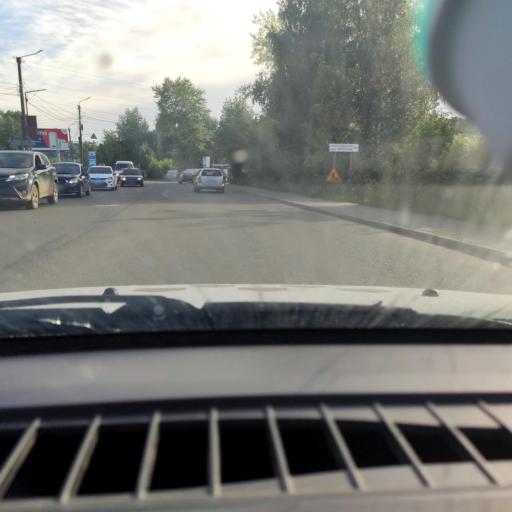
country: RU
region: Kirov
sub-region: Kirovo-Chepetskiy Rayon
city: Kirov
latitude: 58.6207
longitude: 49.6349
